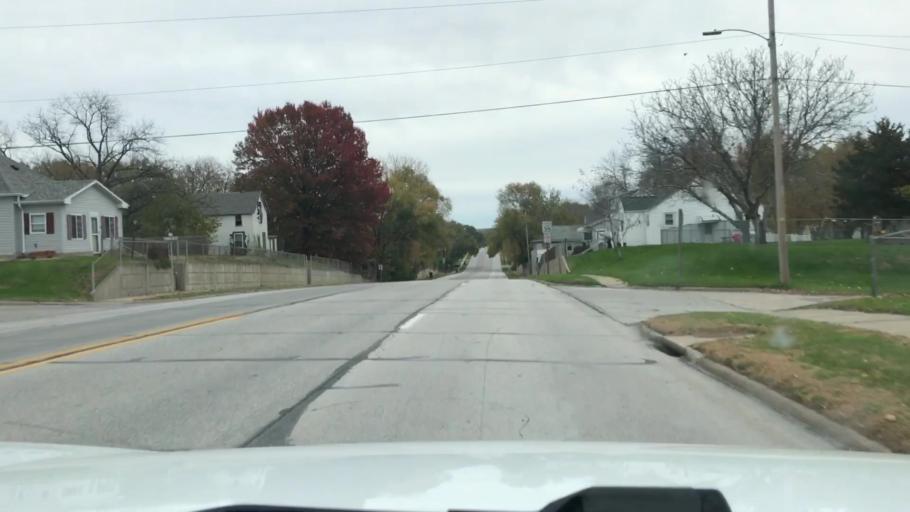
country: US
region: Iowa
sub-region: Lee County
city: Keokuk
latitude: 40.3904
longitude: -91.4069
